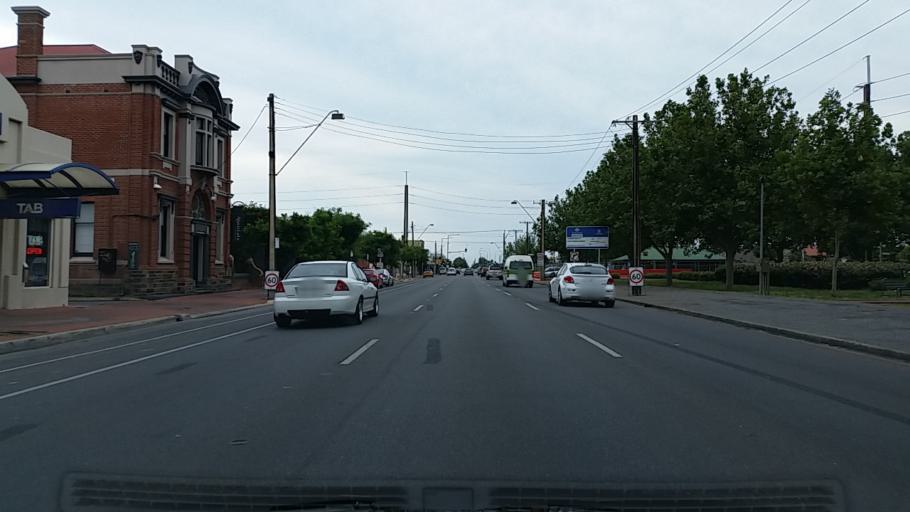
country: AU
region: South Australia
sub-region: City of West Torrens
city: Thebarton
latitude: -34.9046
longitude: 138.5706
